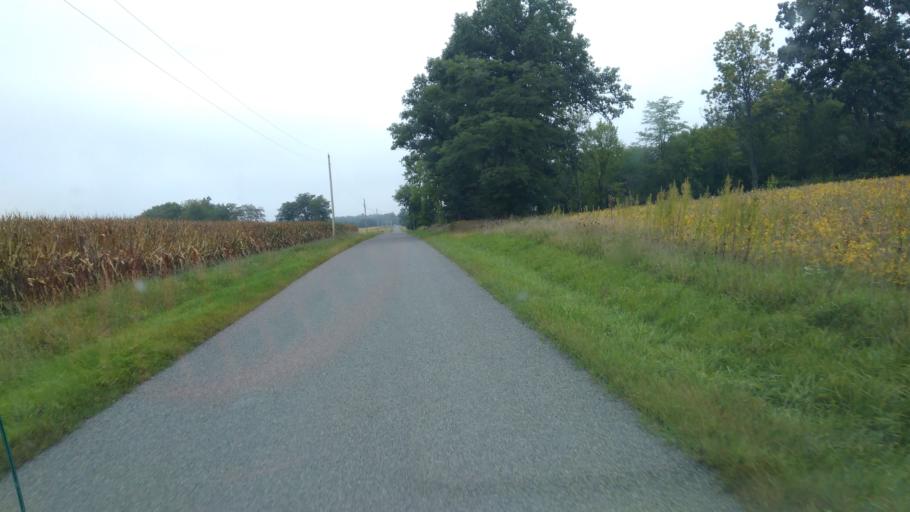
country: US
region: Ohio
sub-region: Logan County
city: Northwood
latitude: 40.4539
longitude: -83.5666
